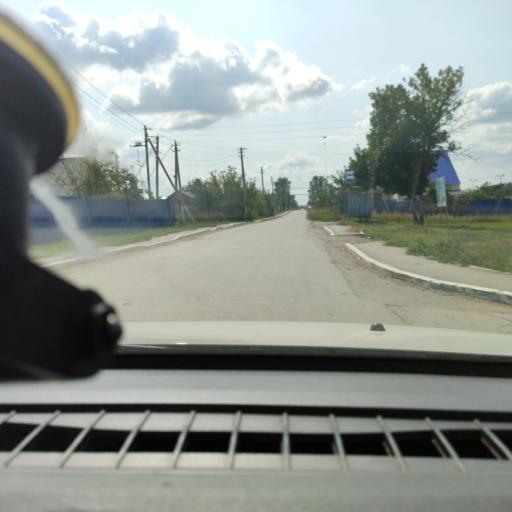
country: RU
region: Samara
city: Chapayevsk
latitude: 53.0141
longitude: 49.7483
